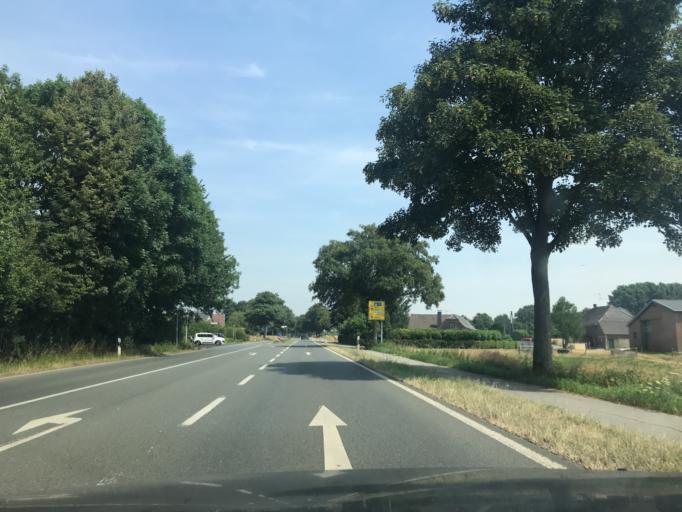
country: DE
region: North Rhine-Westphalia
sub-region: Regierungsbezirk Dusseldorf
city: Issum
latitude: 51.5336
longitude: 6.4314
